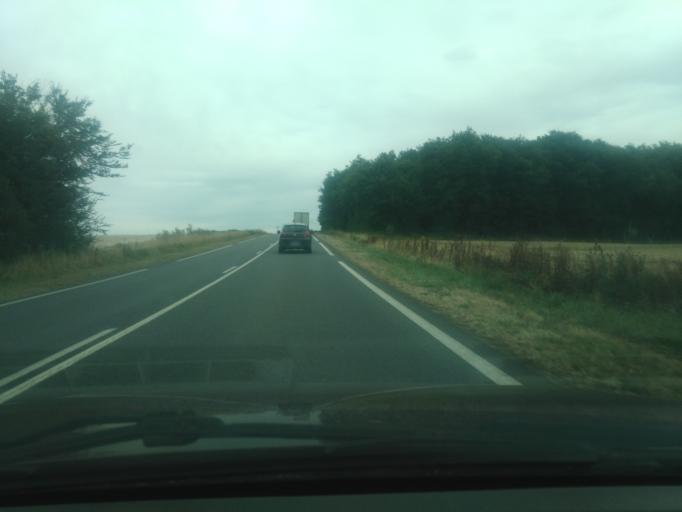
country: FR
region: Poitou-Charentes
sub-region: Departement de la Vienne
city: Saint-Savin
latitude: 46.5732
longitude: 0.8056
